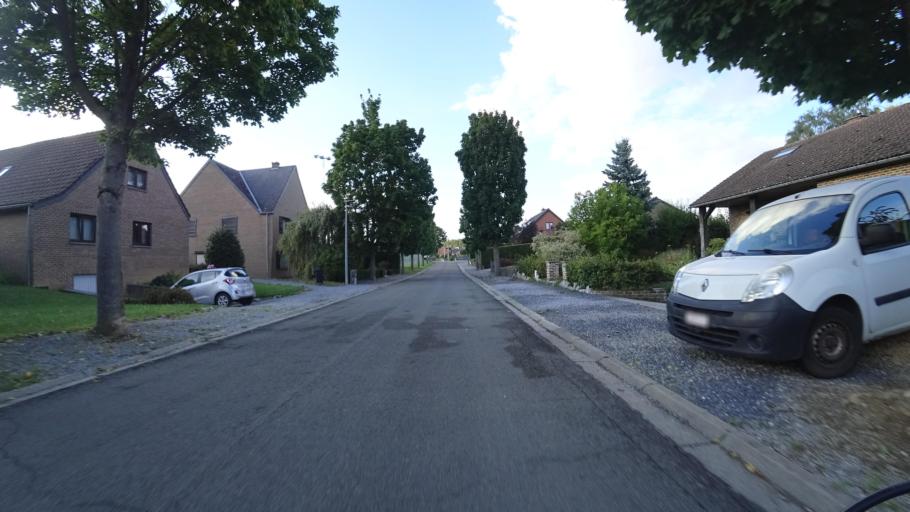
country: BE
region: Wallonia
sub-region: Province de Namur
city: Namur
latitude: 50.4687
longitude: 4.8214
